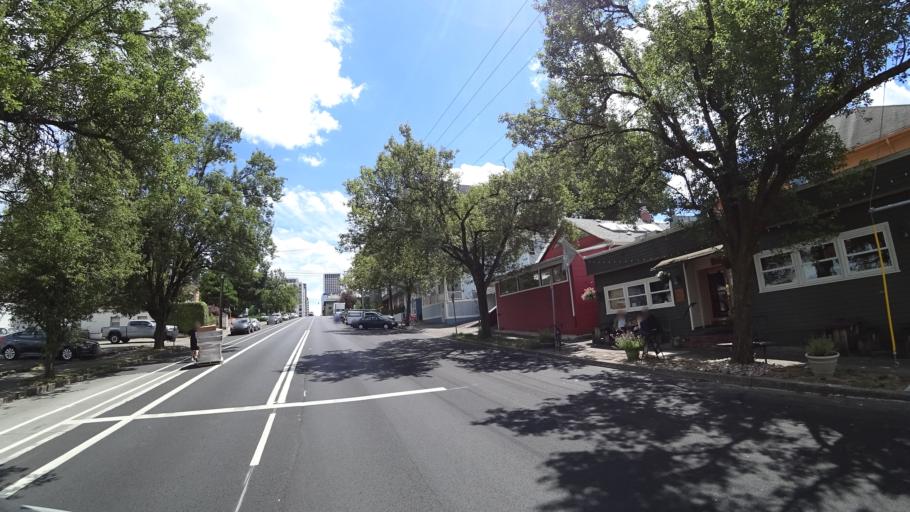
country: US
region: Oregon
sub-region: Multnomah County
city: Portland
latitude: 45.5176
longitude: -122.6902
